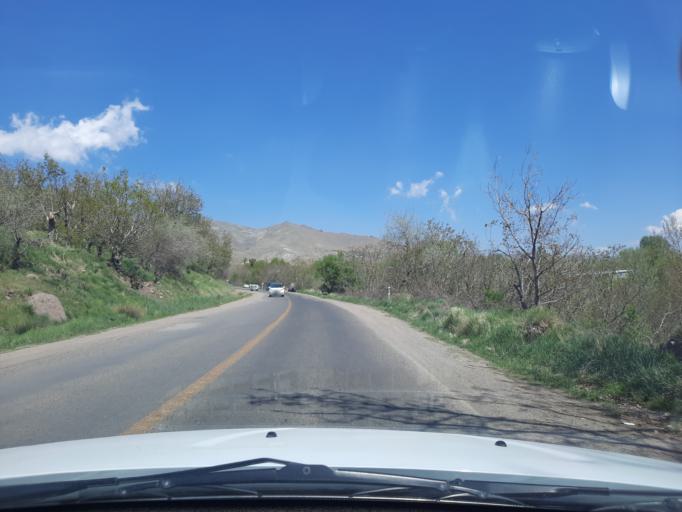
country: IR
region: Qazvin
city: Qazvin
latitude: 36.3431
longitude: 50.1745
